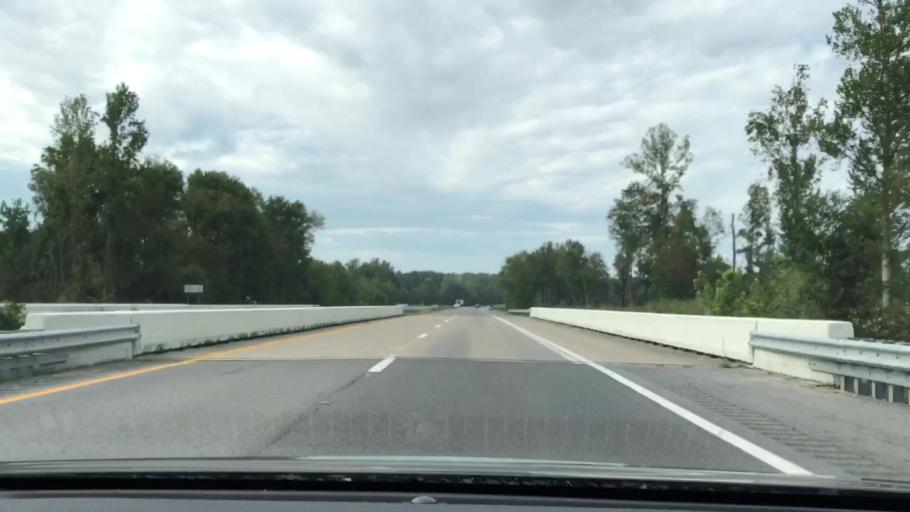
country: US
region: Kentucky
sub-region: Marshall County
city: Benton
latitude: 36.8077
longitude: -88.4928
